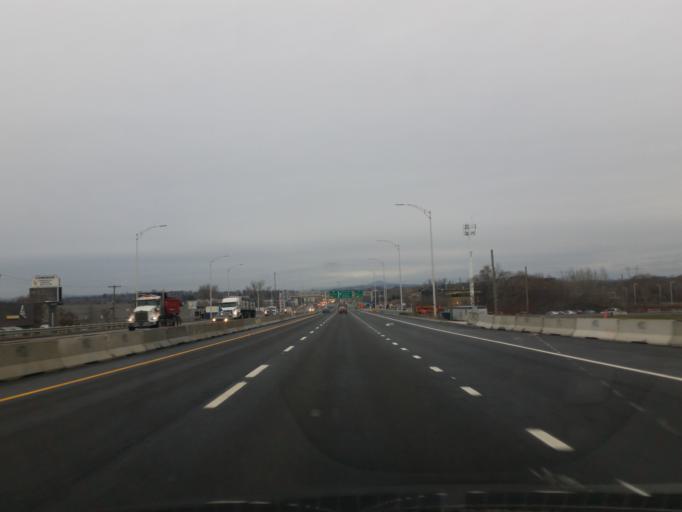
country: CA
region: Quebec
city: L'Ancienne-Lorette
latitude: 46.7994
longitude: -71.3222
